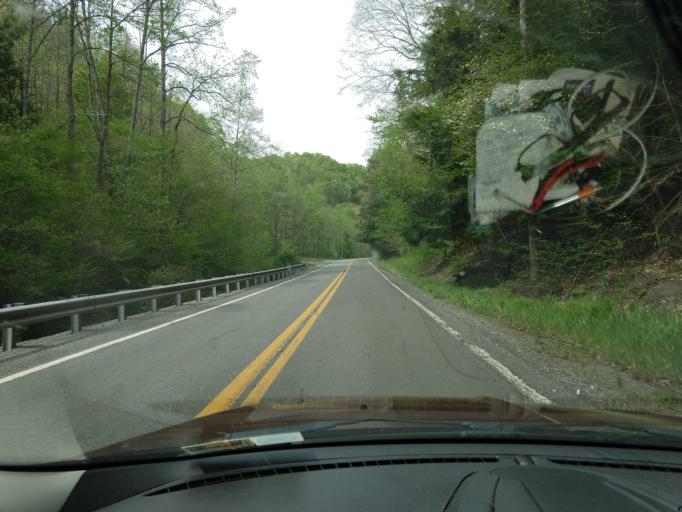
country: US
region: West Virginia
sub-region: McDowell County
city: Welch
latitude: 37.3470
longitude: -81.6678
